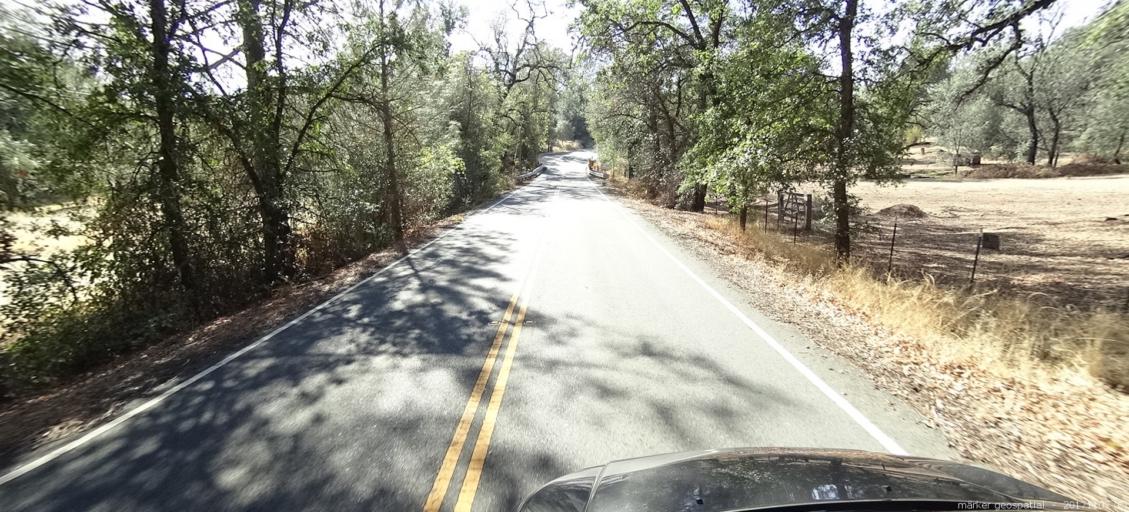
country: US
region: California
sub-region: Shasta County
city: Shasta
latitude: 40.4956
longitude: -122.5468
